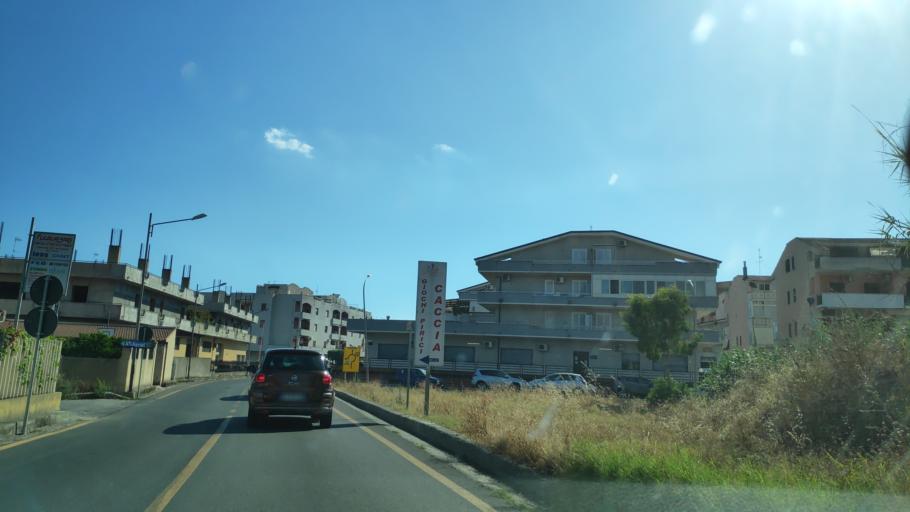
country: IT
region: Calabria
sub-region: Provincia di Reggio Calabria
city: Caulonia Marina
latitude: 38.3464
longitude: 16.4678
